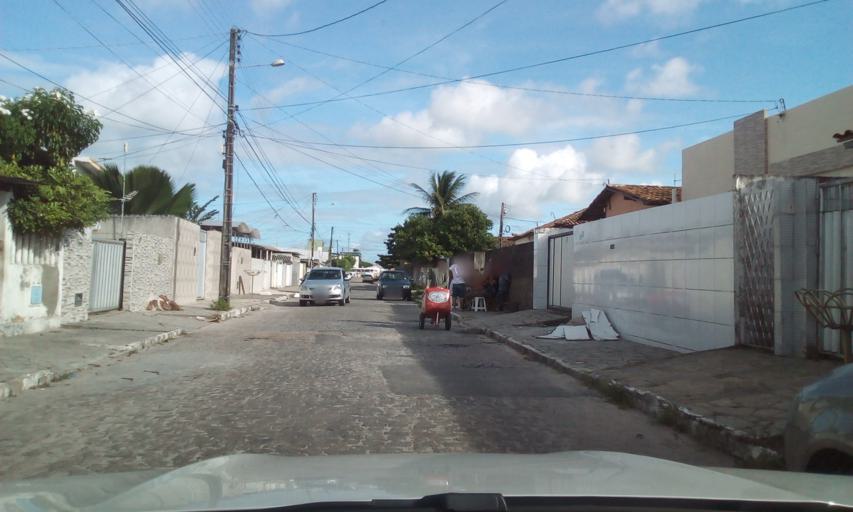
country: BR
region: Paraiba
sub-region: Joao Pessoa
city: Joao Pessoa
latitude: -7.1769
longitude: -34.8393
